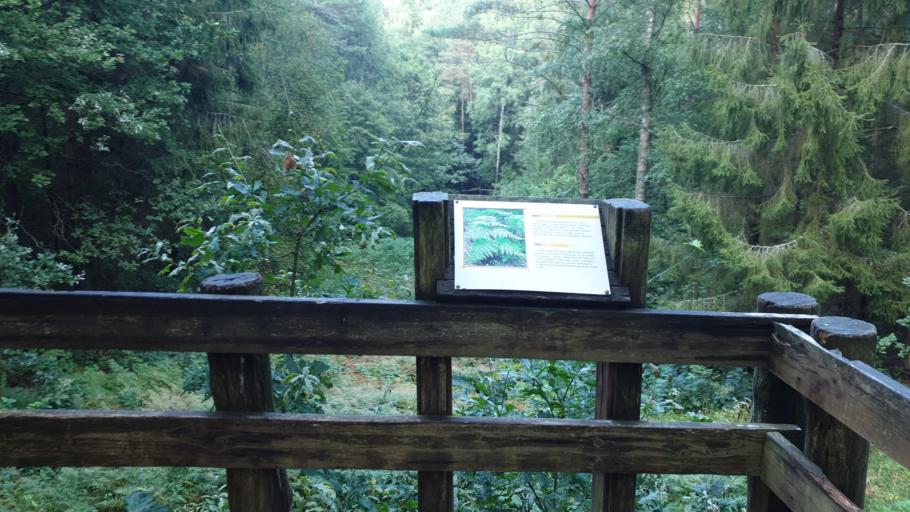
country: LT
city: Trakai
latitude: 54.6478
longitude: 24.9651
